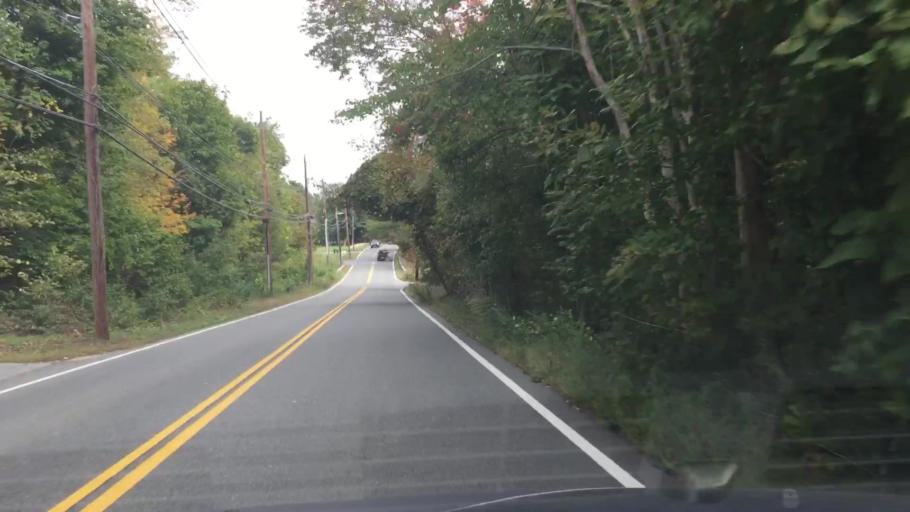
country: US
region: Massachusetts
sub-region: Middlesex County
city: Tewksbury
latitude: 42.6729
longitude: -71.2286
